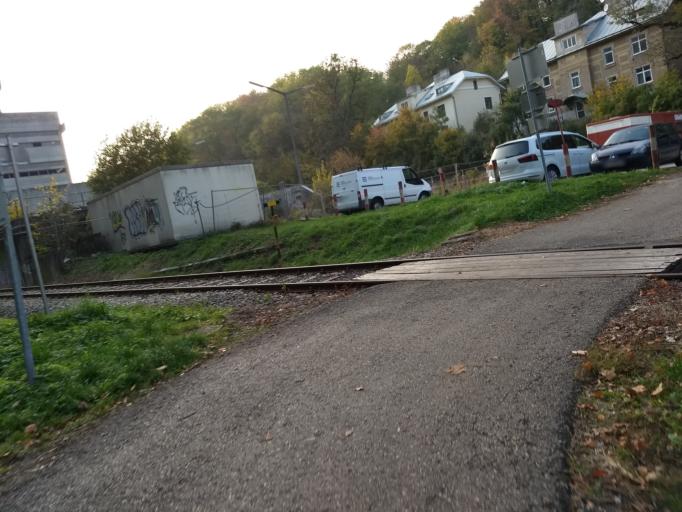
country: AT
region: Lower Austria
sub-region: Politischer Bezirk Modling
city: Giesshubl
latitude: 48.1269
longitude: 16.2295
